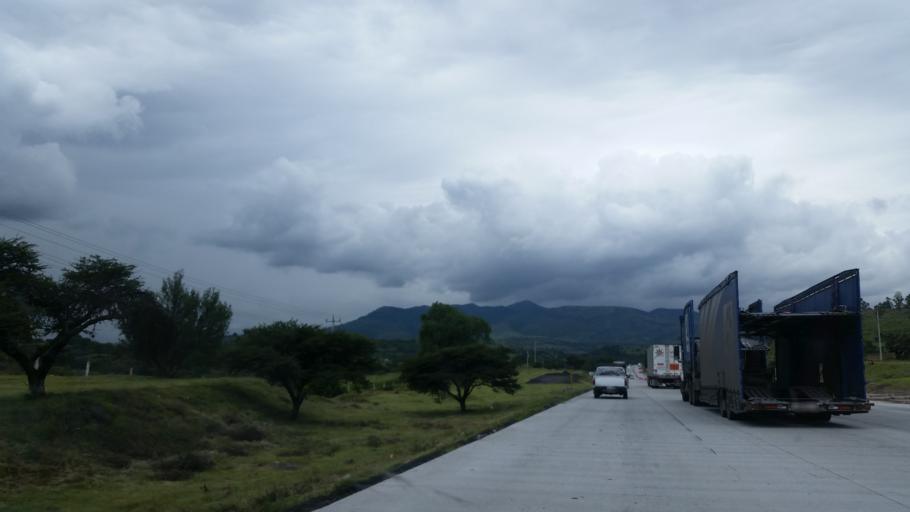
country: MX
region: Hidalgo
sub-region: Tepeji del Rio de Ocampo
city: Cantera de Villagran
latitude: 19.8657
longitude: -99.3227
